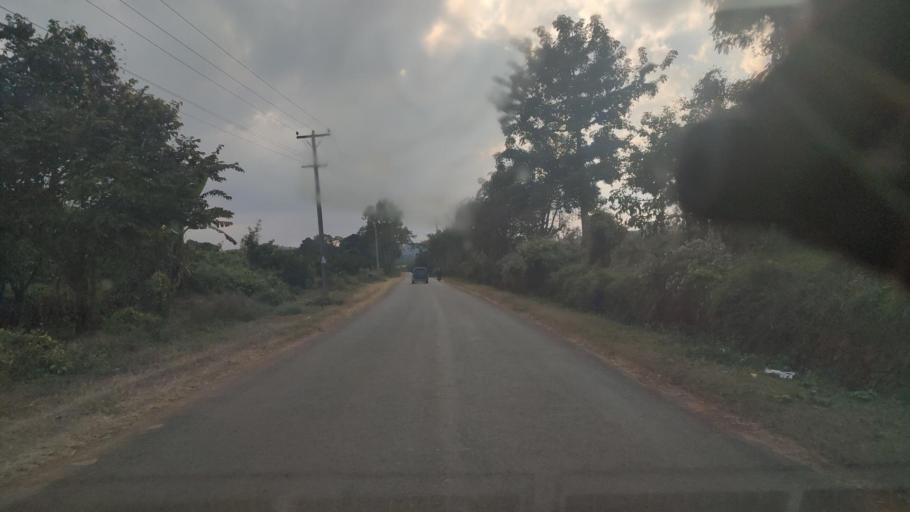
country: MM
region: Shan
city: Taunggyi
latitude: 21.3484
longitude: 96.8735
